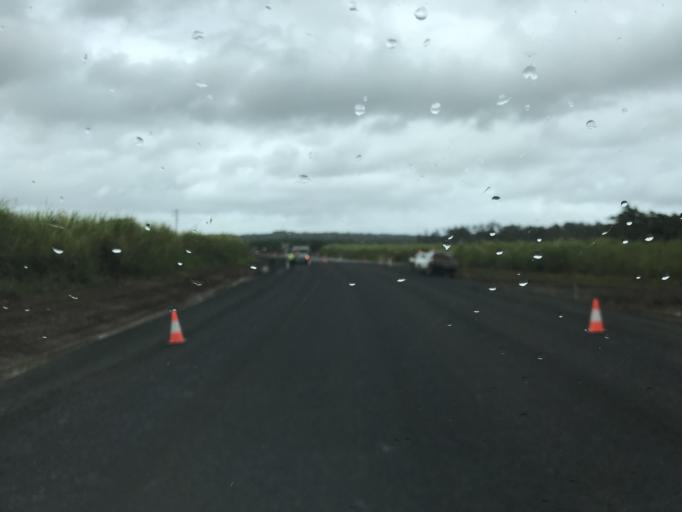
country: AU
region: Queensland
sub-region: Cassowary Coast
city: Innisfail
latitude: -17.5006
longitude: 145.9840
